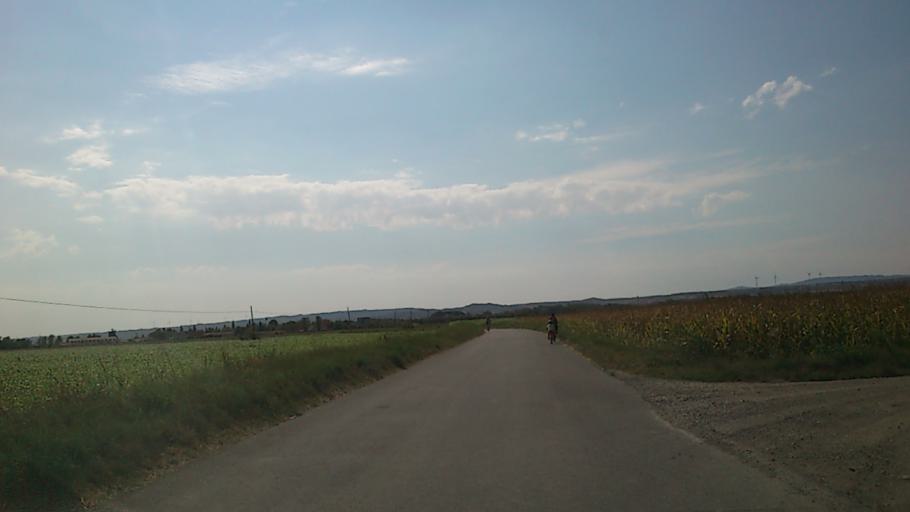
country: ES
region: Aragon
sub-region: Provincia de Zaragoza
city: Puebla de Alfinden
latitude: 41.6161
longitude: -0.7602
